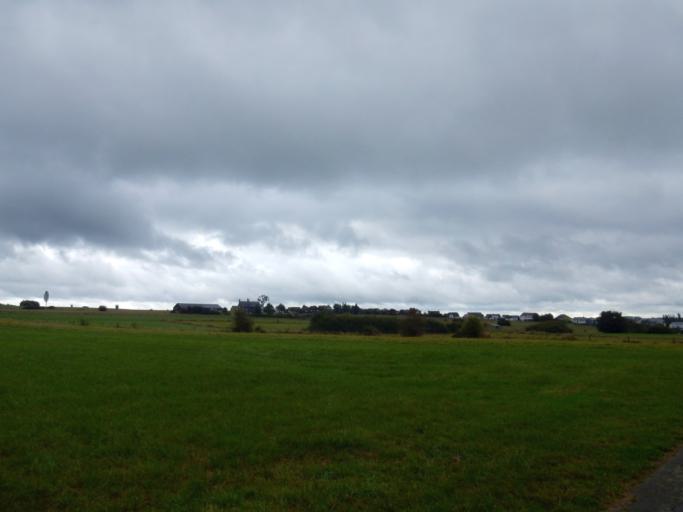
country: LU
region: Luxembourg
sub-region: Canton de Capellen
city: Kehlen
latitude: 49.6802
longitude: 6.0146
